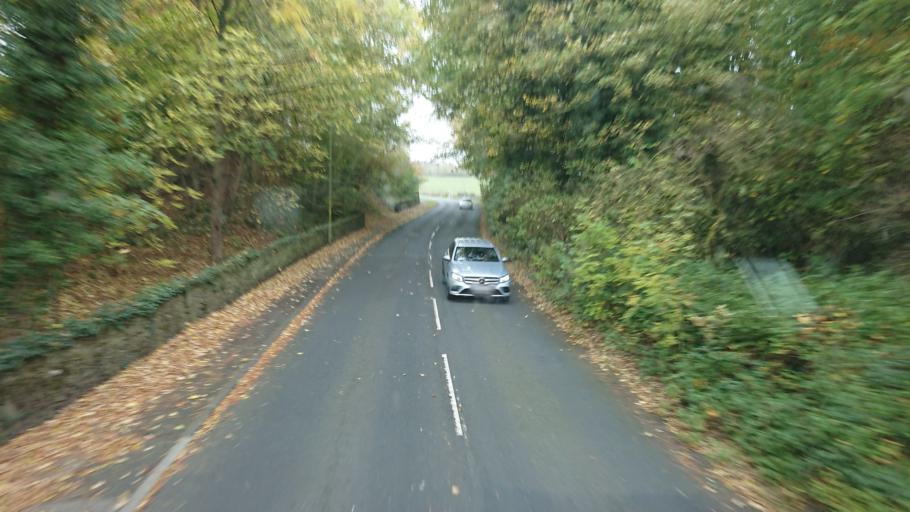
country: GB
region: England
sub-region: North Yorkshire
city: Skipton
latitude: 53.9673
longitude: -2.0236
